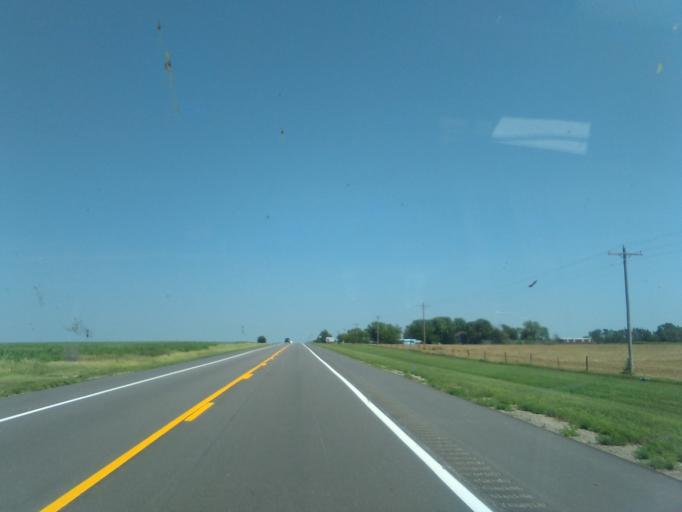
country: US
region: Nebraska
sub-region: Red Willow County
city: McCook
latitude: 40.2972
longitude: -100.6495
